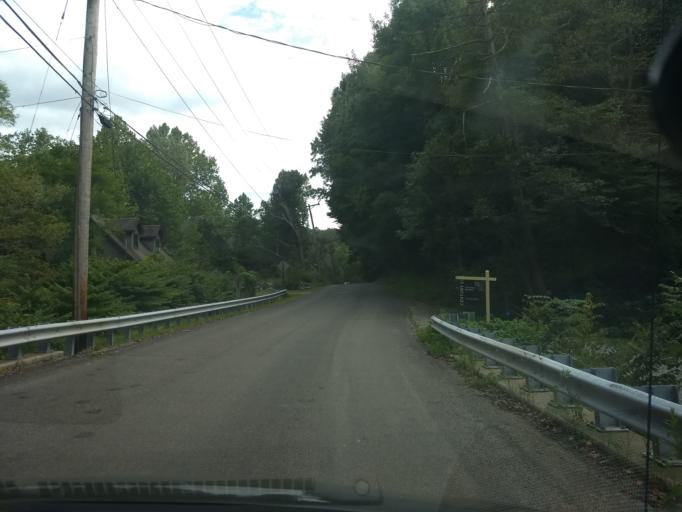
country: US
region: Pennsylvania
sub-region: Westmoreland County
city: Level Green
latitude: 40.4181
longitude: -79.7219
